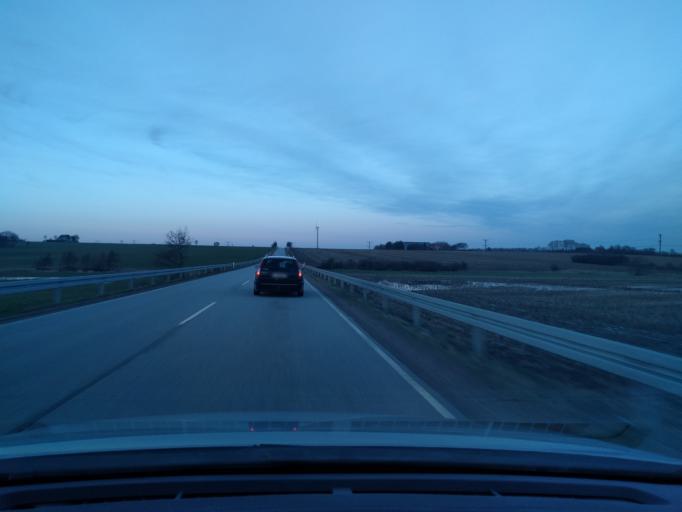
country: DK
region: South Denmark
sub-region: Vejen Kommune
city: Rodding
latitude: 55.3302
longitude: 9.1534
